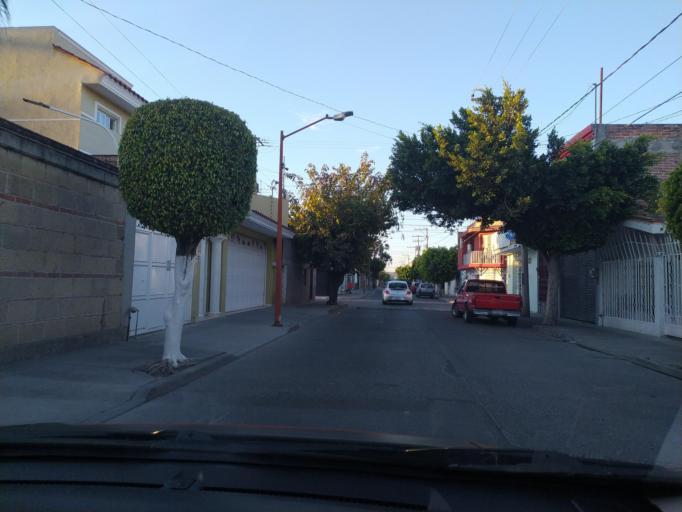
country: MX
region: Guanajuato
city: San Francisco del Rincon
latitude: 21.0116
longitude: -101.8540
